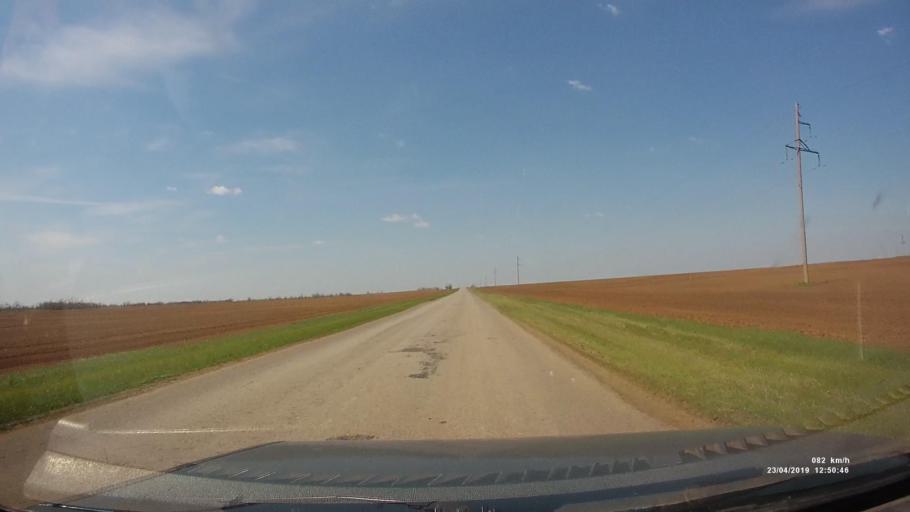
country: RU
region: Kalmykiya
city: Yashalta
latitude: 46.5485
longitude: 42.6315
